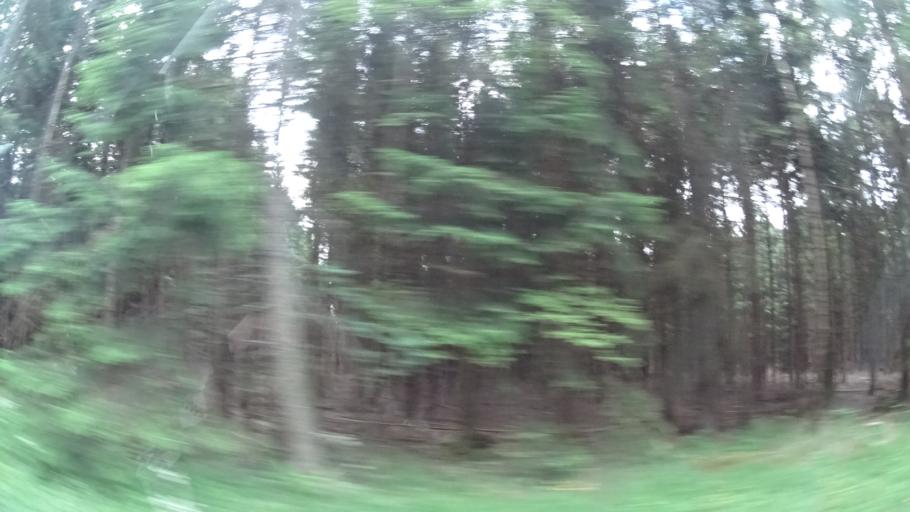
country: DE
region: Hesse
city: Michelstadt
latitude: 49.6860
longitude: 9.0828
